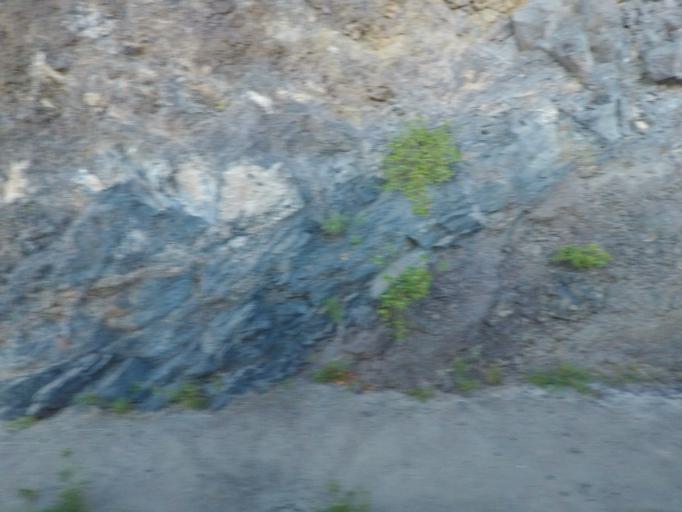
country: ES
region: Canary Islands
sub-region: Provincia de Santa Cruz de Tenerife
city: Alajero
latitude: 28.0548
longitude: -17.2008
